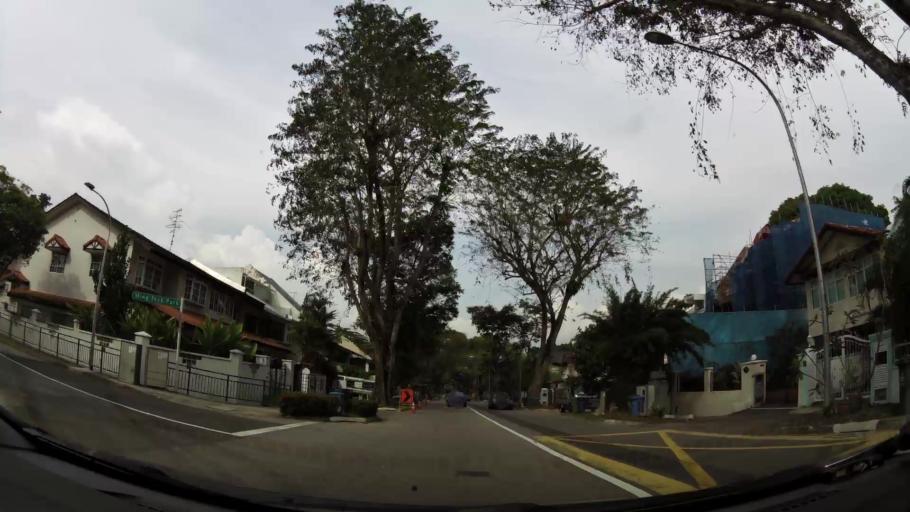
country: SG
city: Singapore
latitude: 1.3194
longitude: 103.7888
